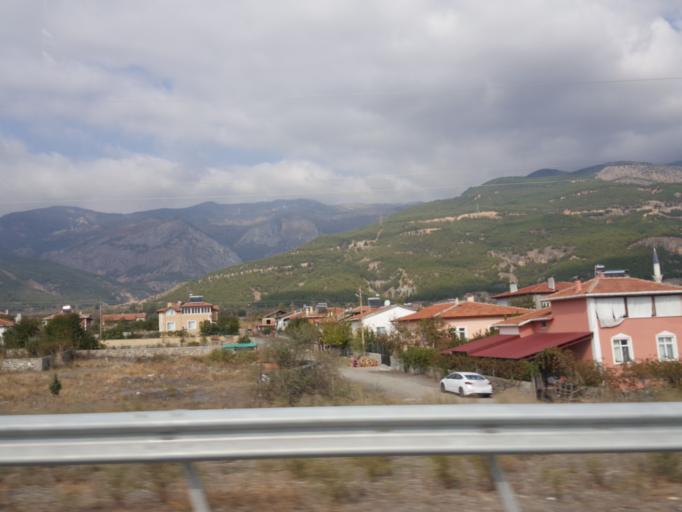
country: TR
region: Corum
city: Hacihamza
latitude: 41.1301
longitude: 34.4257
